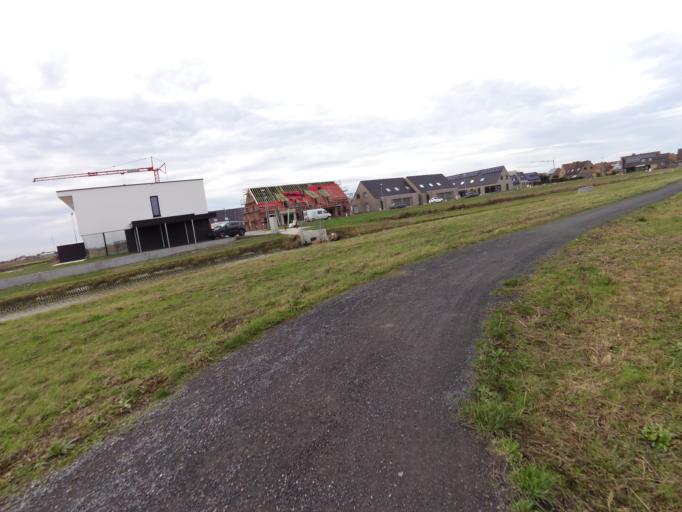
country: BE
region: Flanders
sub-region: Provincie West-Vlaanderen
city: Middelkerke
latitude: 51.1861
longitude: 2.8339
